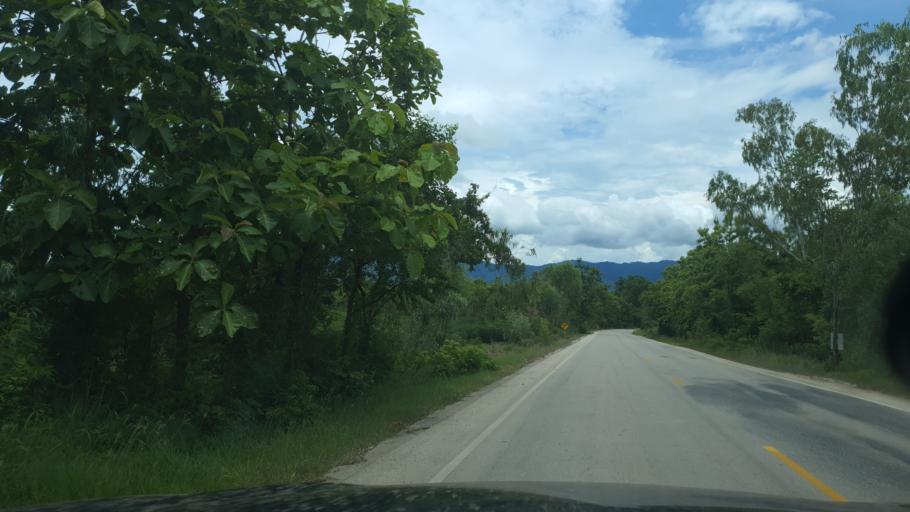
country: TH
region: Lampang
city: Sop Prap
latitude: 17.9271
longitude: 99.3766
